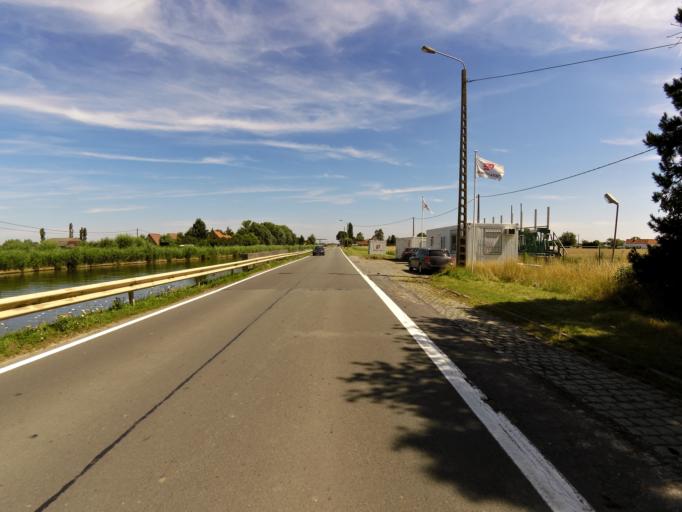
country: BE
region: Flanders
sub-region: Provincie West-Vlaanderen
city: Gistel
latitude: 51.1802
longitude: 2.9556
